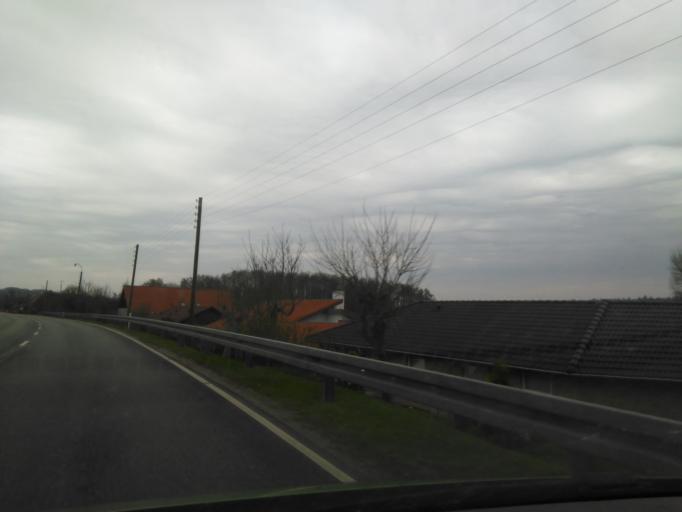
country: DK
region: North Denmark
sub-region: Mariagerfjord Kommune
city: Hadsund
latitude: 56.7070
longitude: 10.1170
